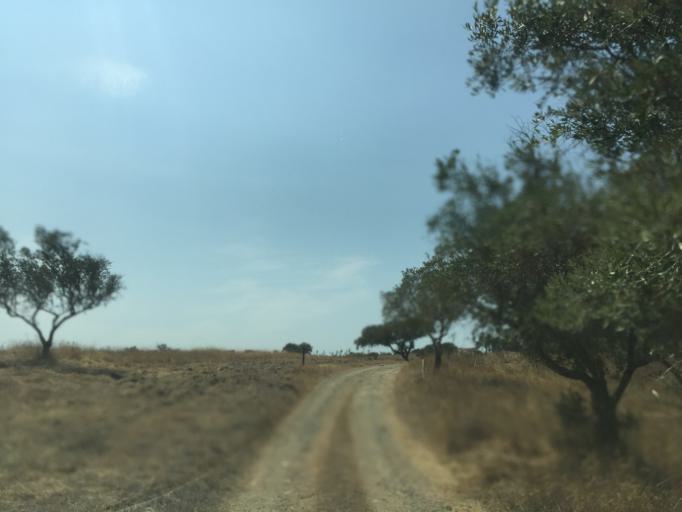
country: PT
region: Setubal
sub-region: Grandola
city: Grandola
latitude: 38.0526
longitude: -8.4494
